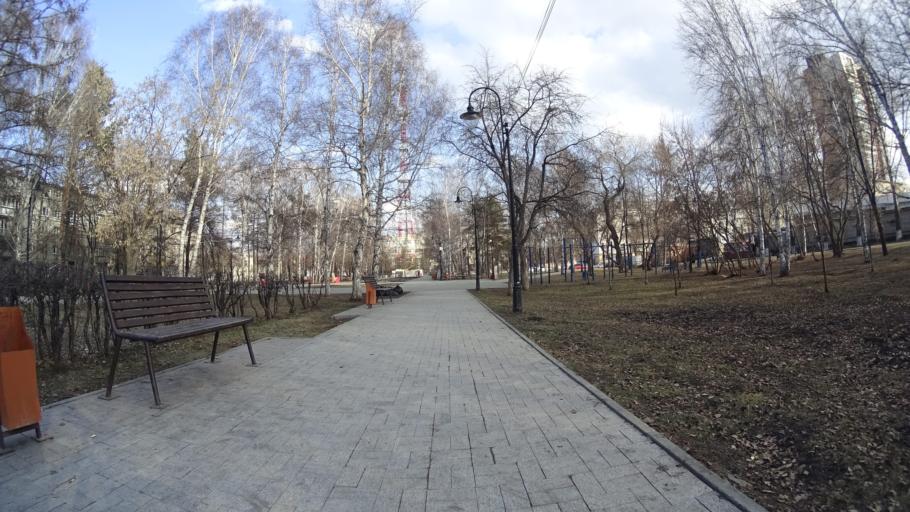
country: RU
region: Chelyabinsk
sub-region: Gorod Chelyabinsk
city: Chelyabinsk
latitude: 55.1437
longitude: 61.3753
